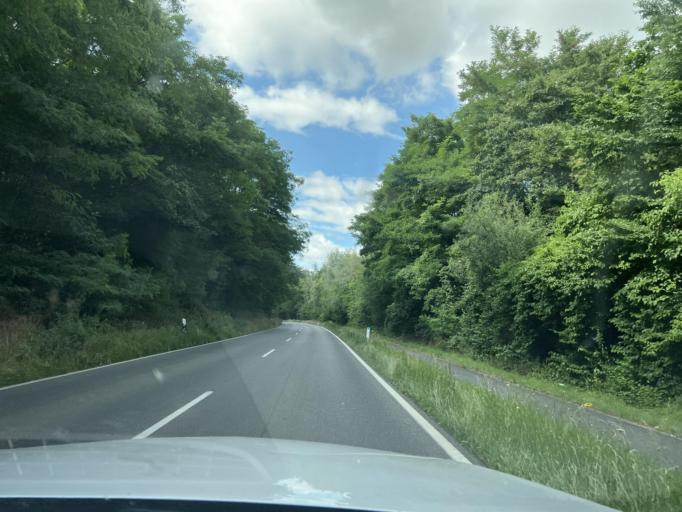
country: DE
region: North Rhine-Westphalia
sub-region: Regierungsbezirk Koln
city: Bergheim
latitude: 50.9569
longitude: 6.6907
